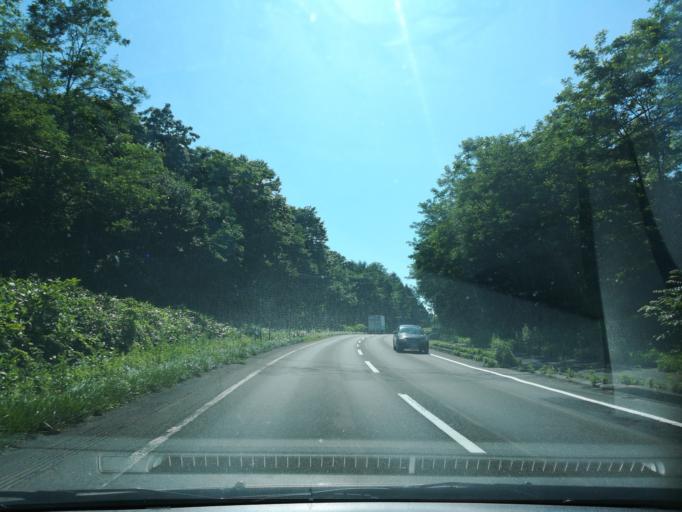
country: JP
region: Hokkaido
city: Chitose
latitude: 42.9164
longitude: 141.9076
